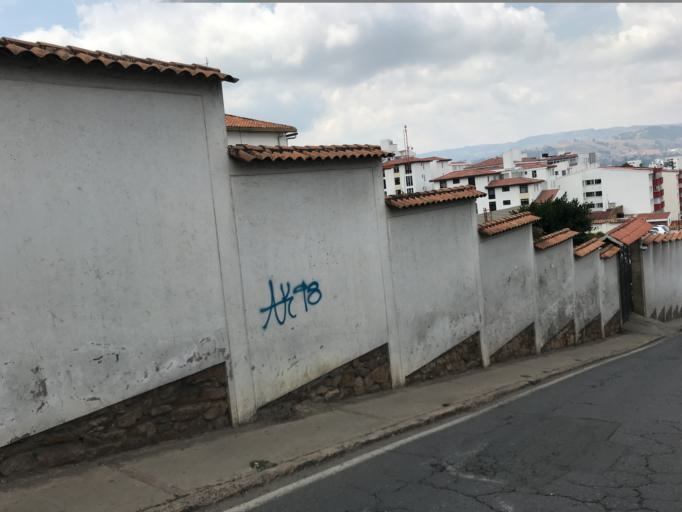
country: CO
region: Boyaca
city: Tunja
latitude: 5.5322
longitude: -73.3588
